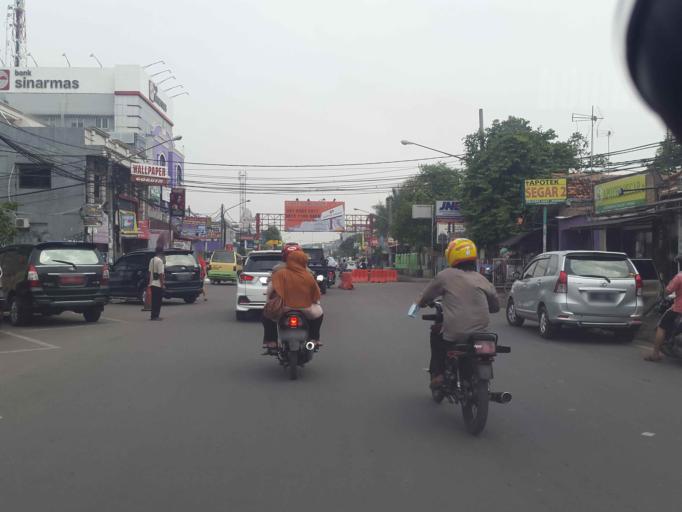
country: ID
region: West Java
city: Cikarang
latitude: -6.3071
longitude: 107.2929
